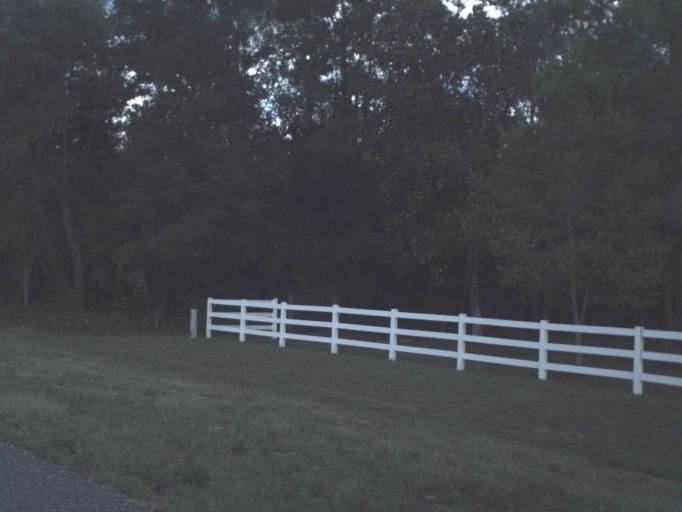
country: US
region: Florida
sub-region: Taylor County
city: Perry
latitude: 30.0410
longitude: -83.5486
